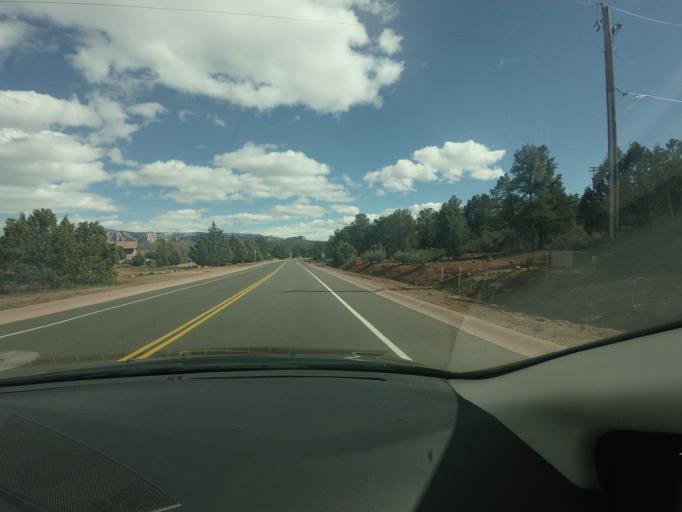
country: US
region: Arizona
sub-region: Yavapai County
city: West Sedona
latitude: 34.8669
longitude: -111.8196
